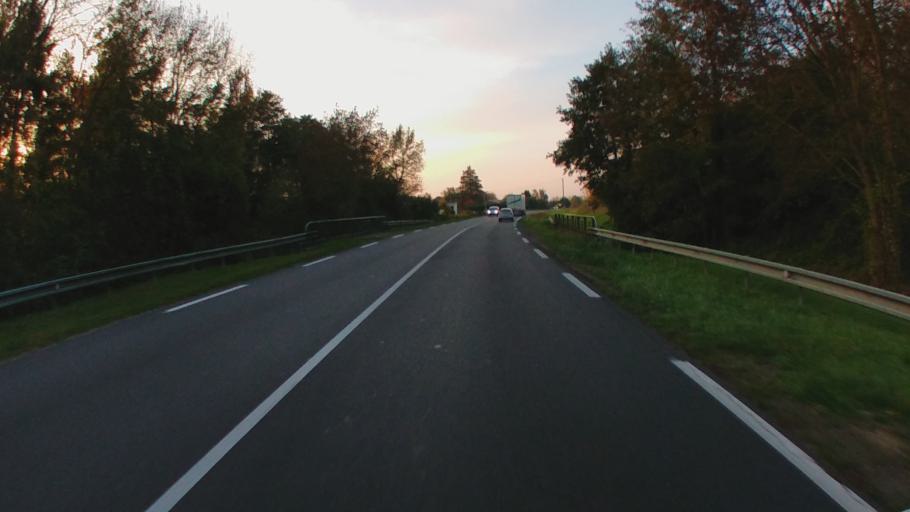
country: FR
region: Pays de la Loire
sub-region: Departement de Maine-et-Loire
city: Jumelles
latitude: 47.3840
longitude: -0.1116
